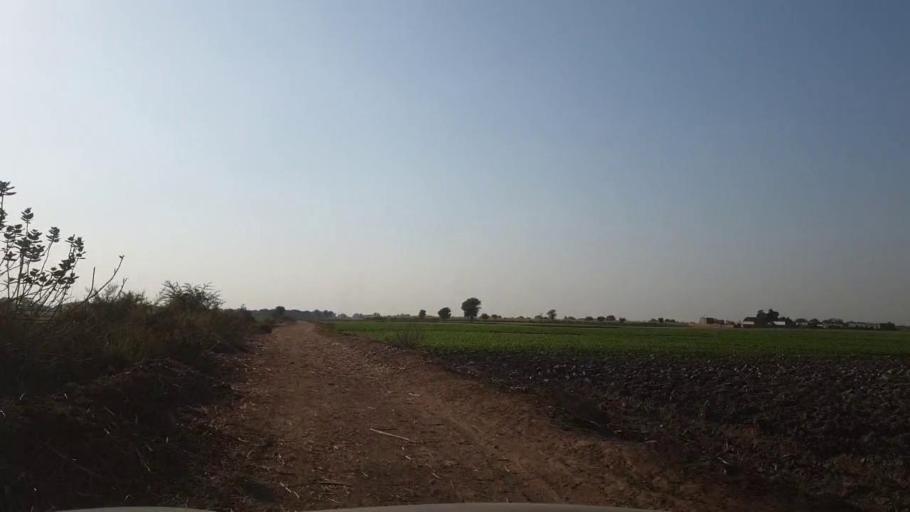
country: PK
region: Sindh
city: Tando Allahyar
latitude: 25.5762
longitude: 68.6552
